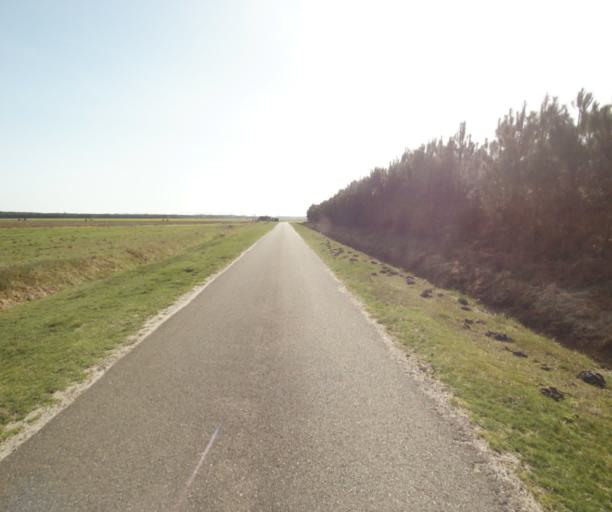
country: FR
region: Aquitaine
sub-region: Departement des Landes
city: Roquefort
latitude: 44.1761
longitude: -0.2512
